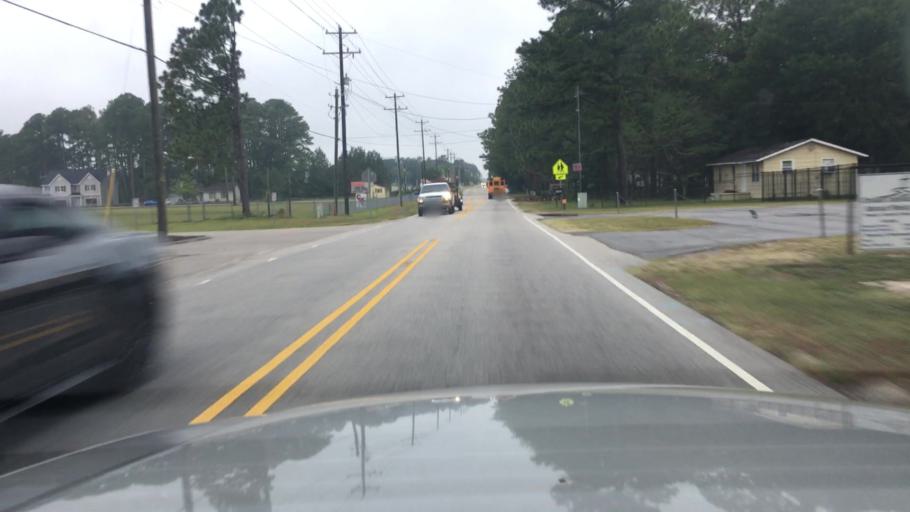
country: US
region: North Carolina
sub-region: Cumberland County
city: Hope Mills
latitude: 34.9767
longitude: -78.9814
